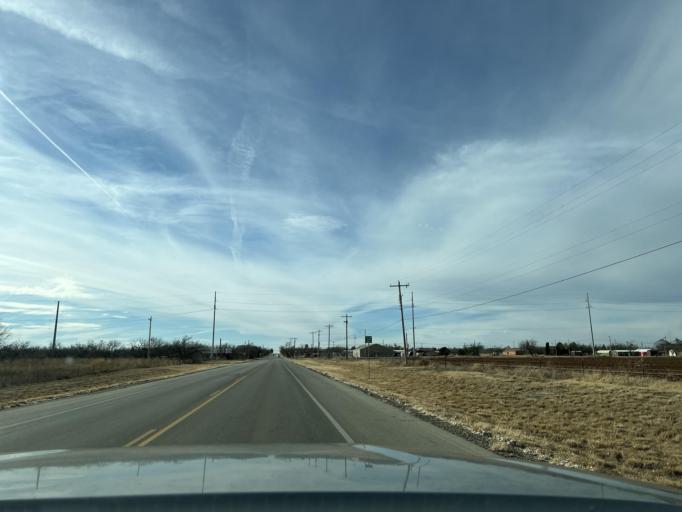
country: US
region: Texas
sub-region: Jones County
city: Anson
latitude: 32.7515
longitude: -99.8851
